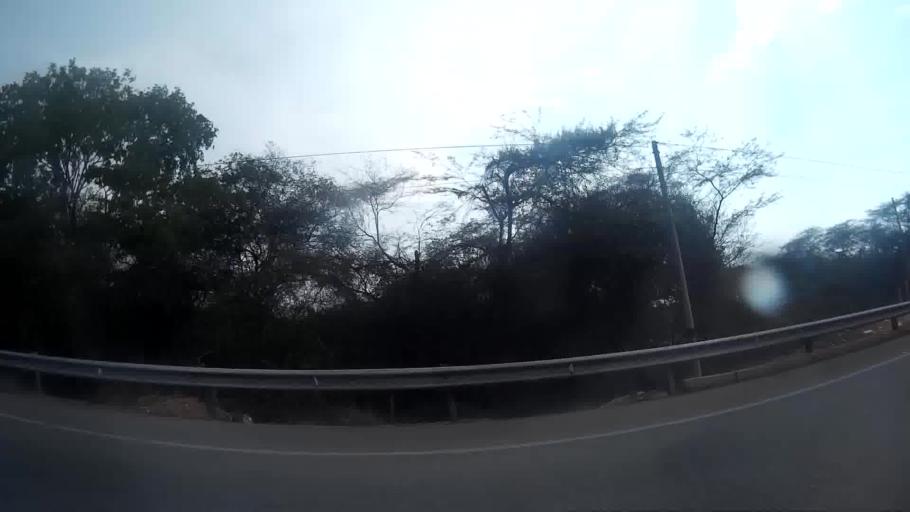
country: CO
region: Magdalena
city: Cienaga
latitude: 11.1042
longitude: -74.2201
